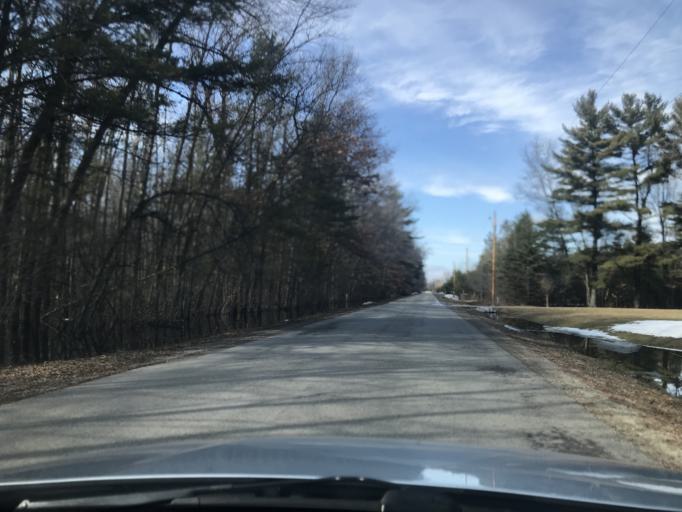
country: US
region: Wisconsin
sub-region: Marinette County
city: Marinette
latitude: 45.0347
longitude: -87.6677
